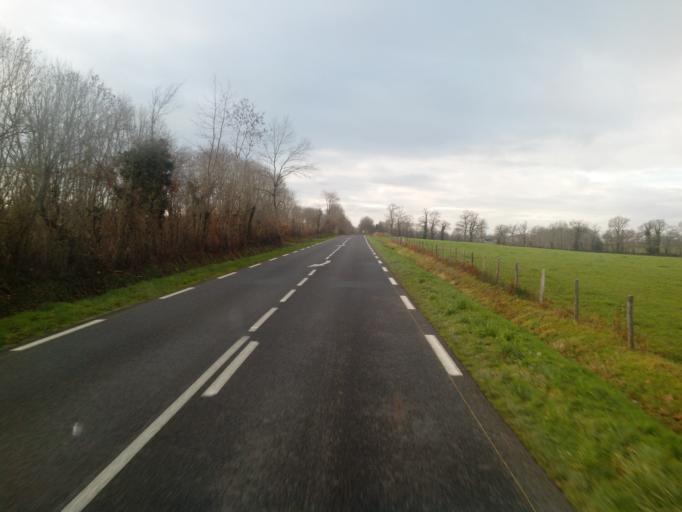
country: FR
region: Limousin
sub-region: Departement de la Haute-Vienne
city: Le Dorat
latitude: 46.2146
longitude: 1.1092
